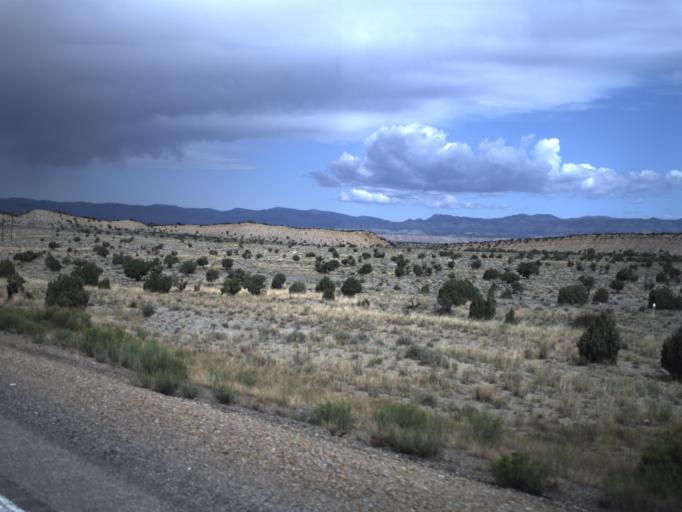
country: US
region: Utah
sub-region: Carbon County
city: Wellington
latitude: 39.5470
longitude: -110.6288
